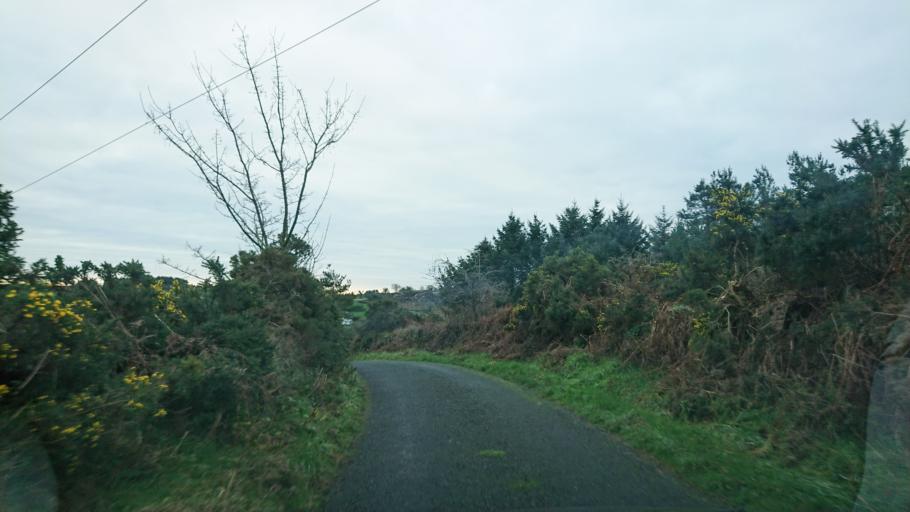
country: IE
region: Leinster
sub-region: Kilkenny
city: Mooncoin
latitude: 52.2148
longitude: -7.2715
